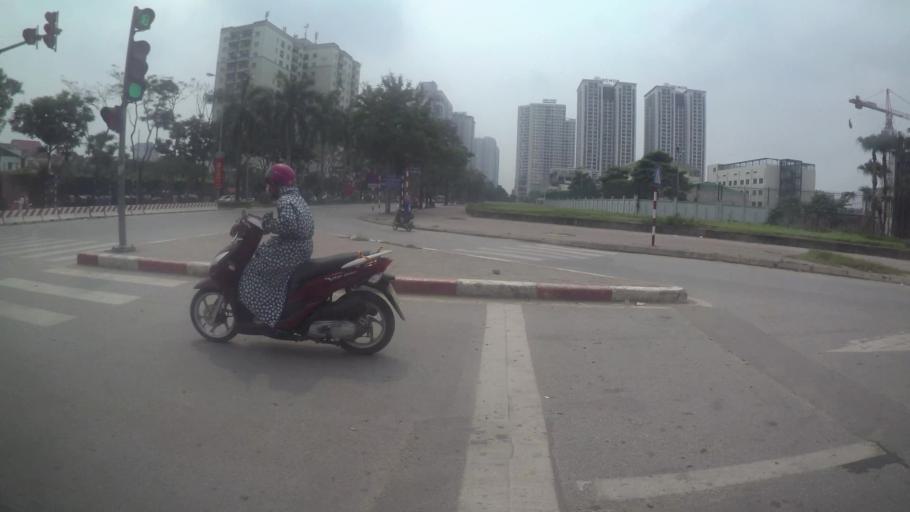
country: VN
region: Ha Noi
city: Cau Dien
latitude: 21.0336
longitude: 105.7698
